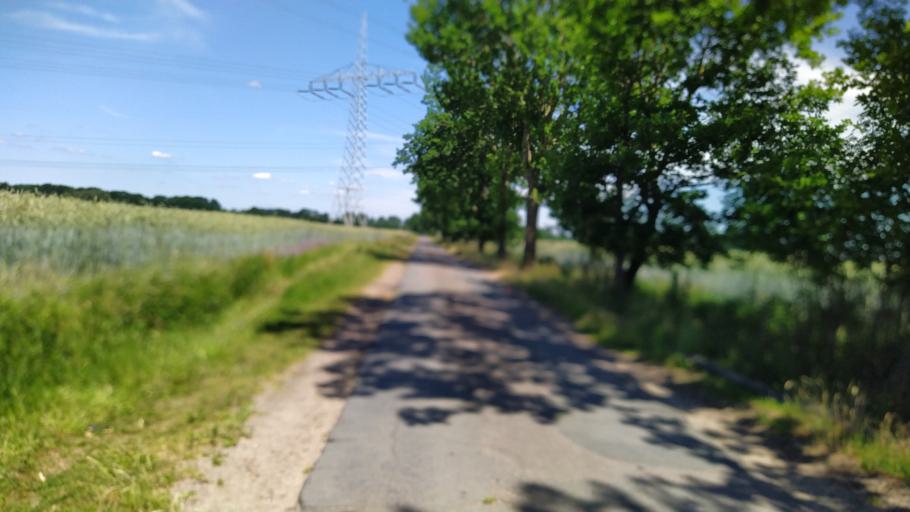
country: DE
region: Lower Saxony
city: Deinste
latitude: 53.5094
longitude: 9.4403
